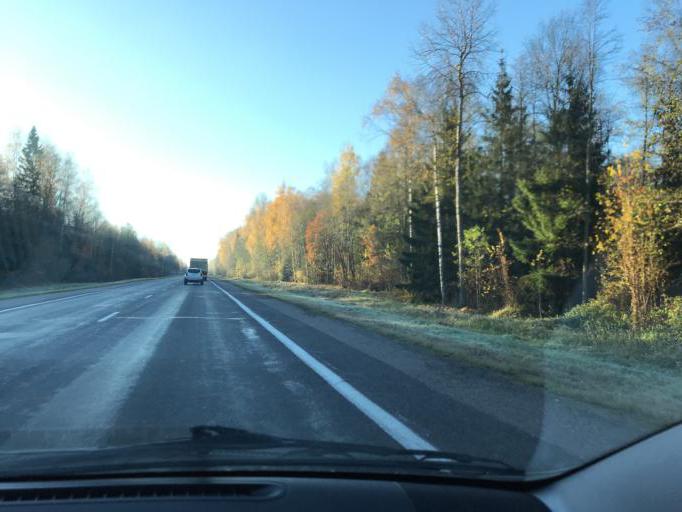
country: BY
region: Vitebsk
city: Vitebsk
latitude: 54.9534
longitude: 30.3590
